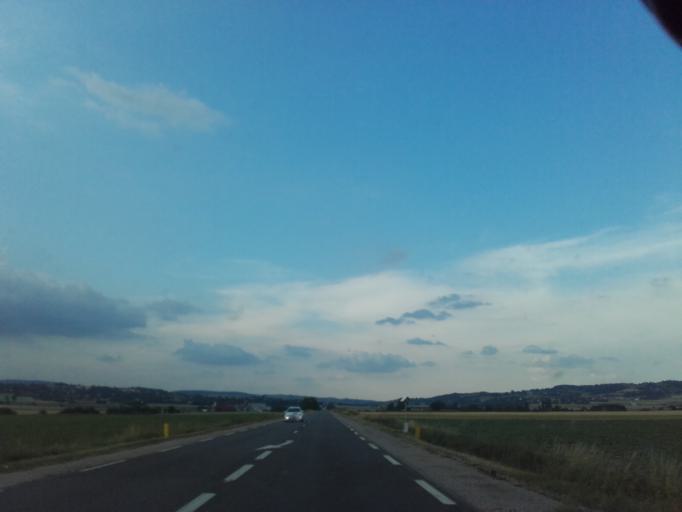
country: FR
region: Rhone-Alpes
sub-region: Departement de l'Isere
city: Auberives-sur-Vareze
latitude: 45.4421
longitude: 4.8207
